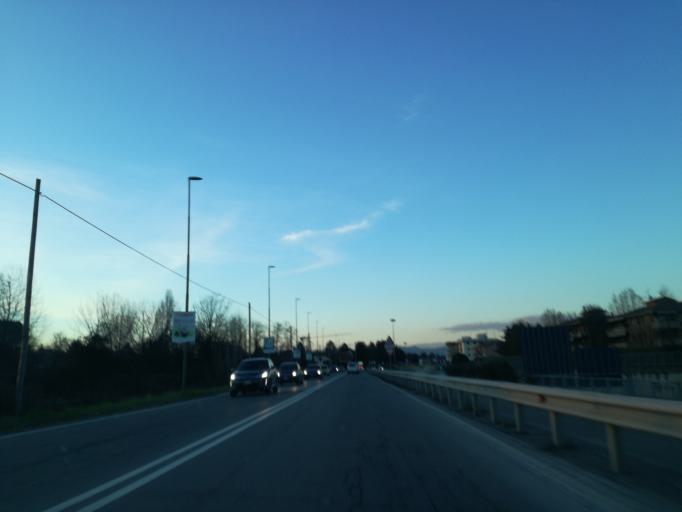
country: IT
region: Lombardy
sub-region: Provincia di Monza e Brianza
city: Vimercate
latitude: 45.6099
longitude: 9.3601
